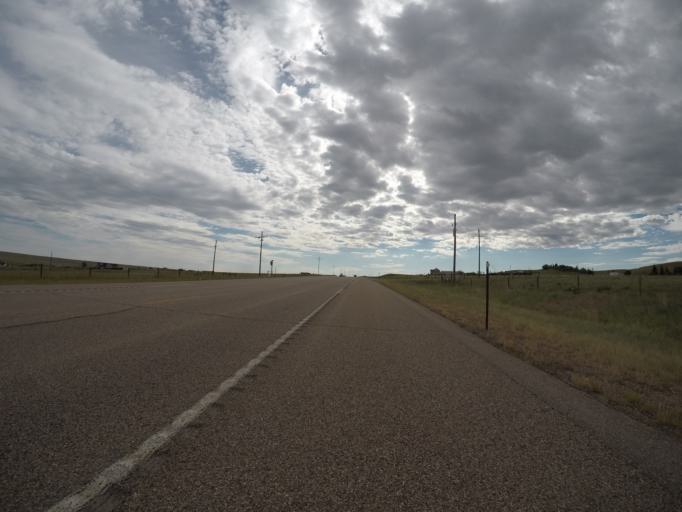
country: US
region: Wyoming
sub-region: Laramie County
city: Cheyenne
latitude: 41.1565
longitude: -105.0496
